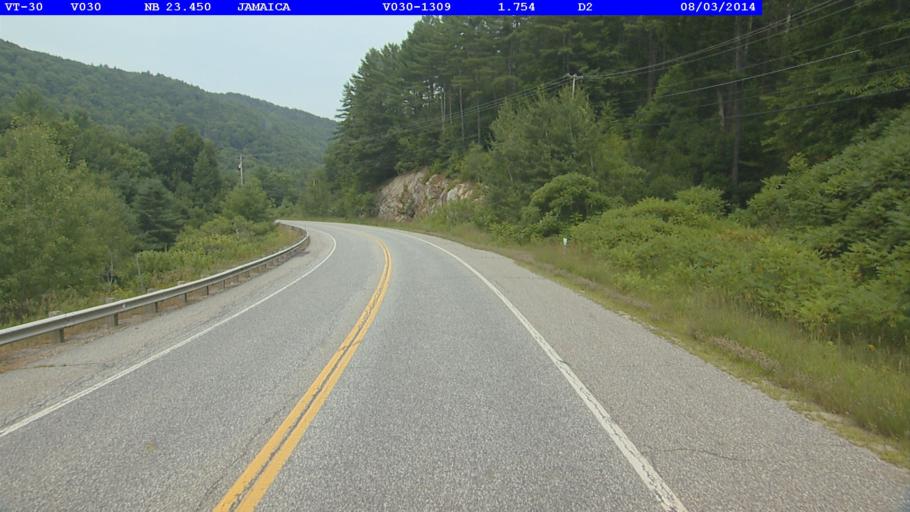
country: US
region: Vermont
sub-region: Windham County
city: Newfane
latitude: 43.0836
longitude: -72.7519
